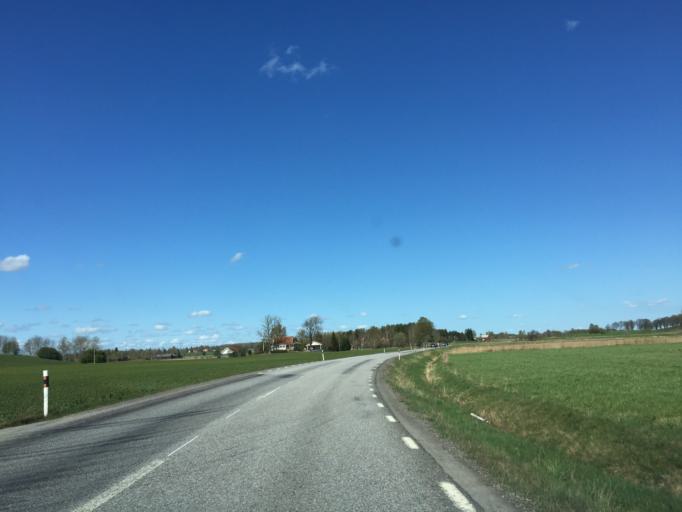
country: SE
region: OErebro
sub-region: Hallsbergs Kommun
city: Skollersta
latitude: 59.1153
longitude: 15.3299
